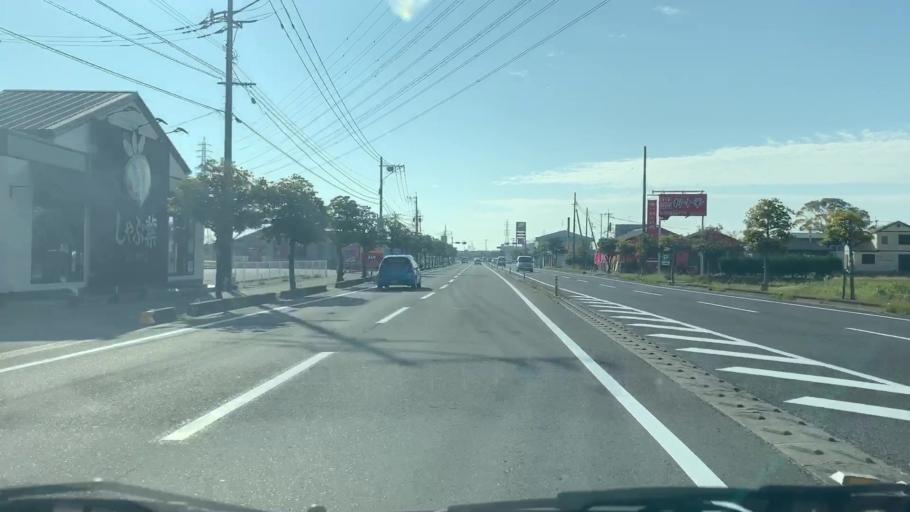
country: JP
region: Saga Prefecture
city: Saga-shi
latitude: 33.3009
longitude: 130.2801
